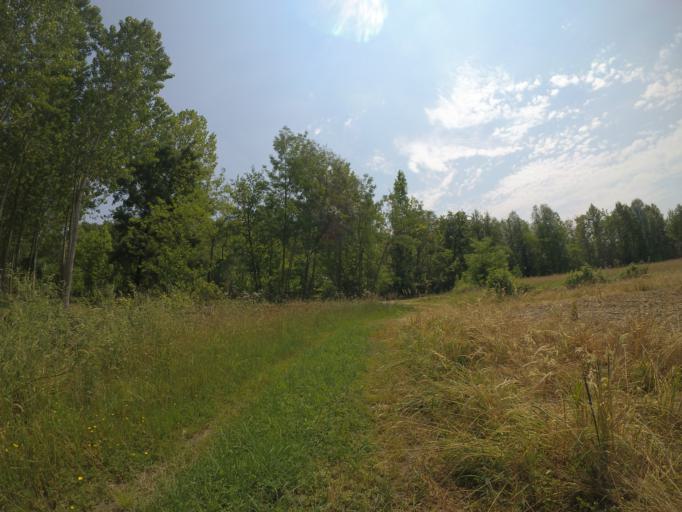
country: IT
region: Friuli Venezia Giulia
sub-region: Provincia di Udine
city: Bertiolo
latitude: 45.9176
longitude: 13.0353
